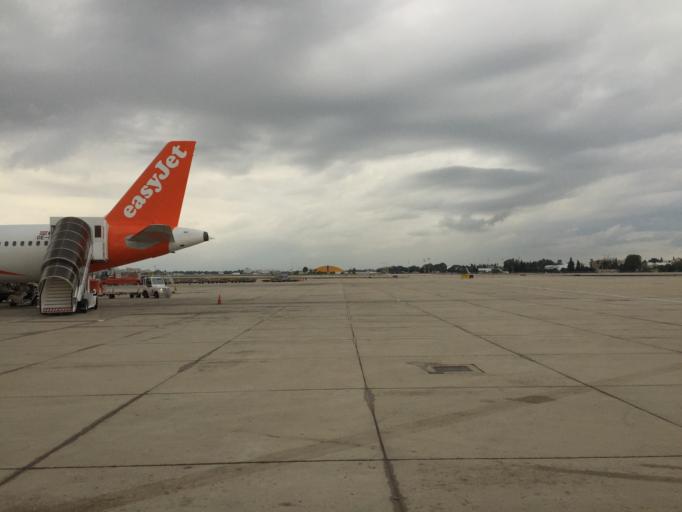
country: IL
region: Central District
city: Yehud
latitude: 31.9961
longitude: 34.8927
